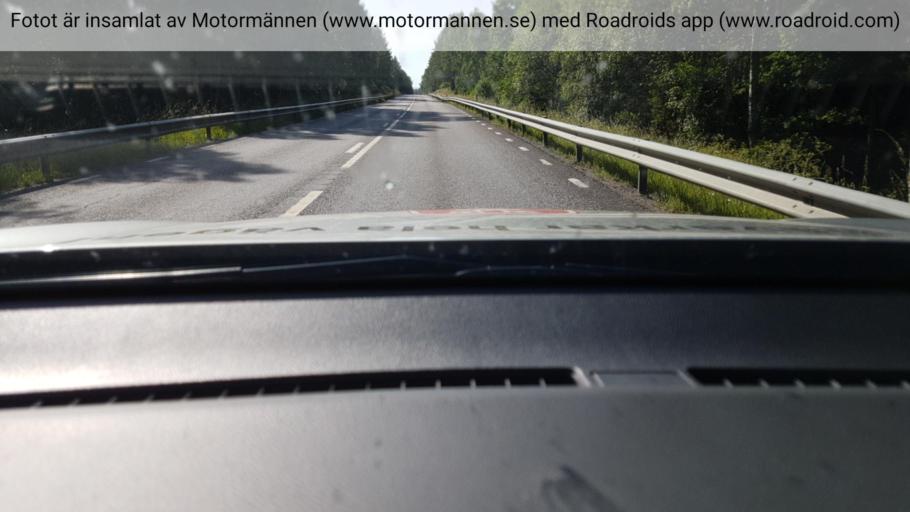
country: SE
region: Vaestra Goetaland
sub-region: Tidaholms Kommun
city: Tidaholm
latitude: 58.2210
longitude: 13.8493
